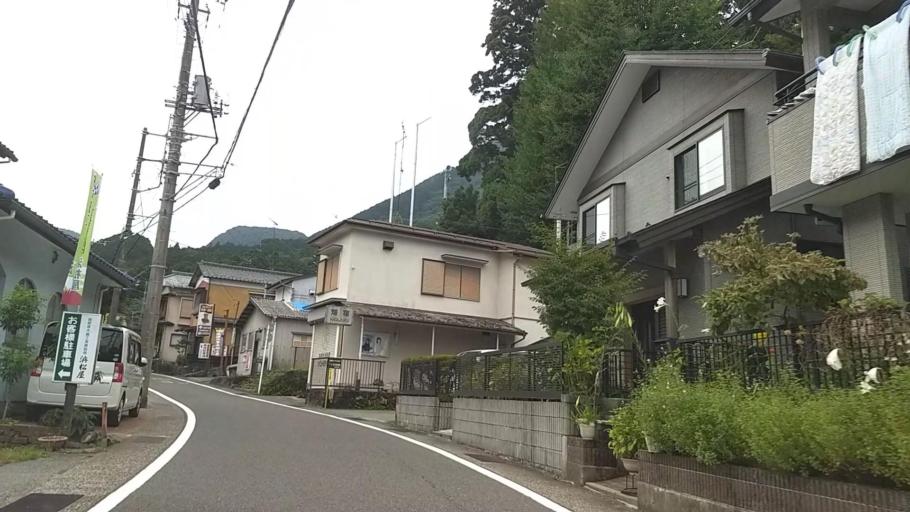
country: JP
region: Kanagawa
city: Hakone
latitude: 35.2132
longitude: 139.0637
